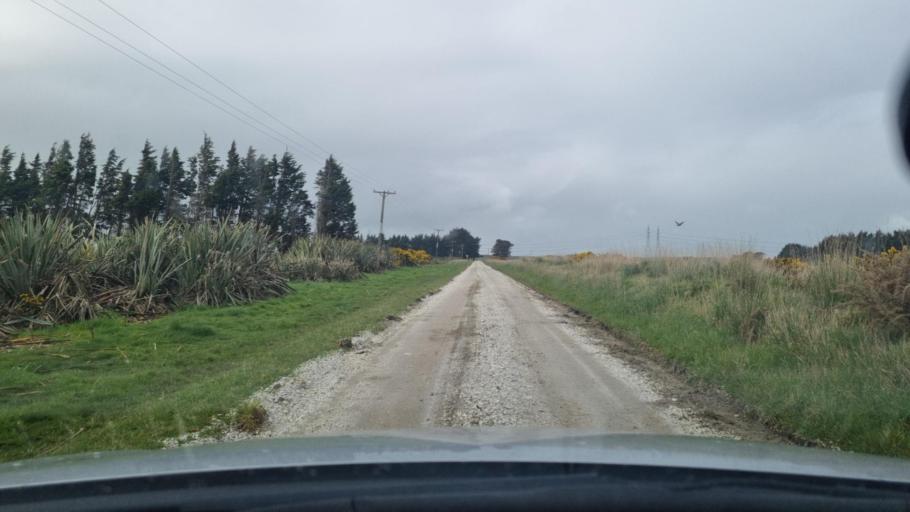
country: NZ
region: Southland
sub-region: Invercargill City
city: Invercargill
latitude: -46.4940
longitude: 168.4238
